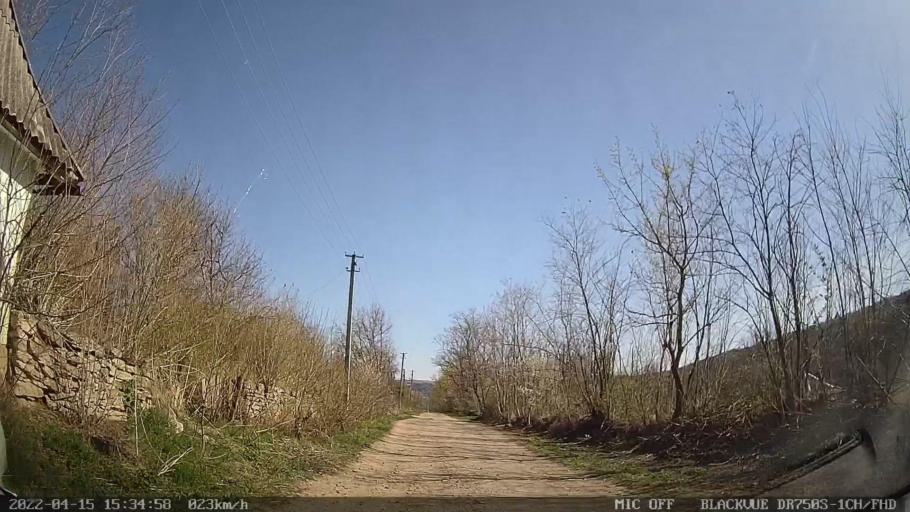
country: MD
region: Raionul Ocnita
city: Otaci
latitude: 48.3461
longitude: 27.9295
